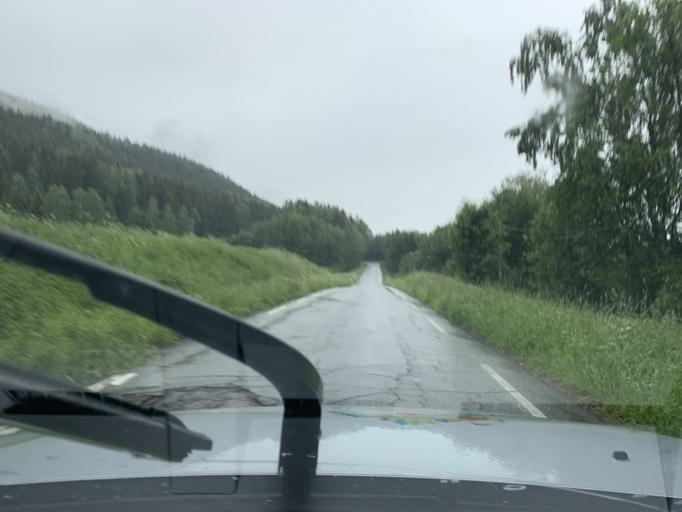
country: NO
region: Oppland
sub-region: Oyer
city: Tretten
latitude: 61.3964
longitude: 10.2354
